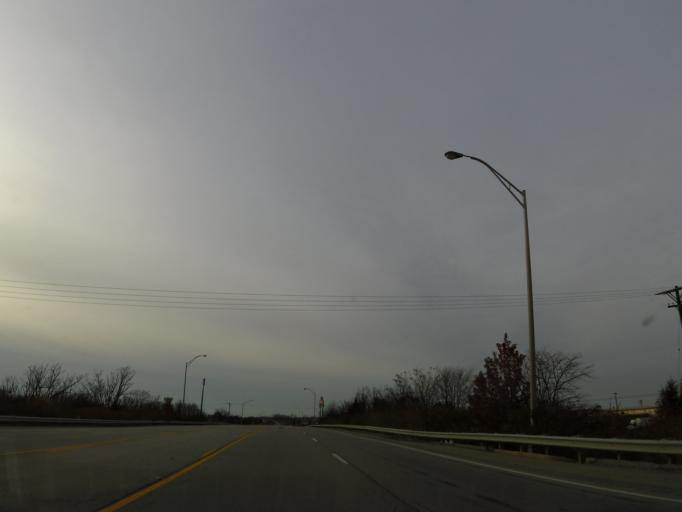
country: US
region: Kentucky
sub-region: Scott County
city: Georgetown
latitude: 38.2734
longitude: -84.5489
